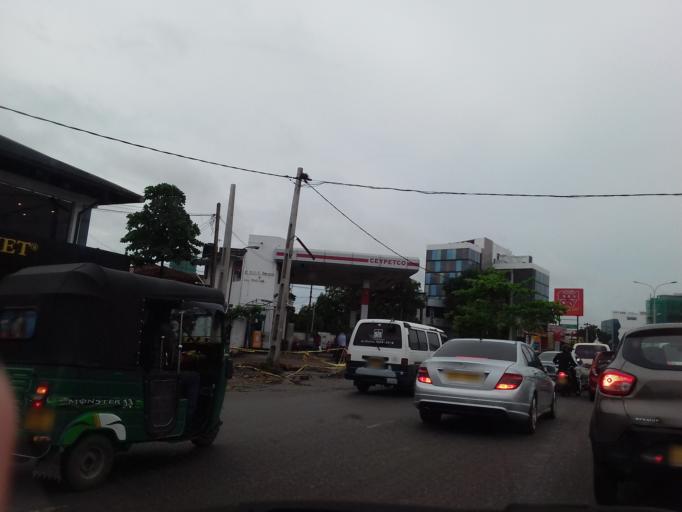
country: LK
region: Western
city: Pita Kotte
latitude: 6.9087
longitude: 79.8982
